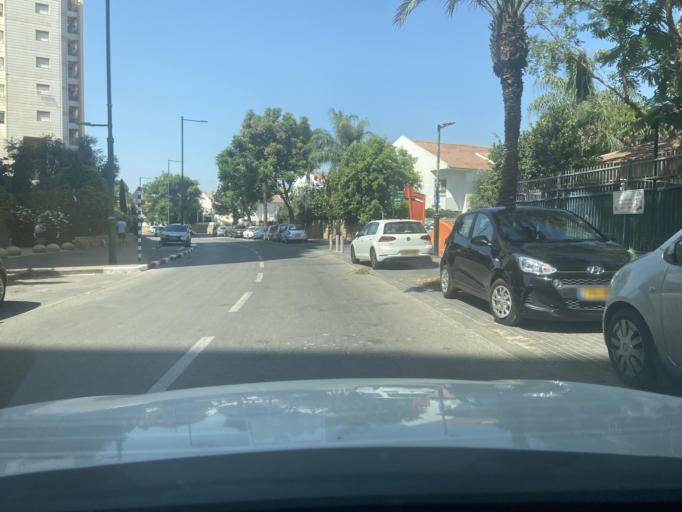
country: IL
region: Central District
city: Yehud
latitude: 32.0352
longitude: 34.8786
